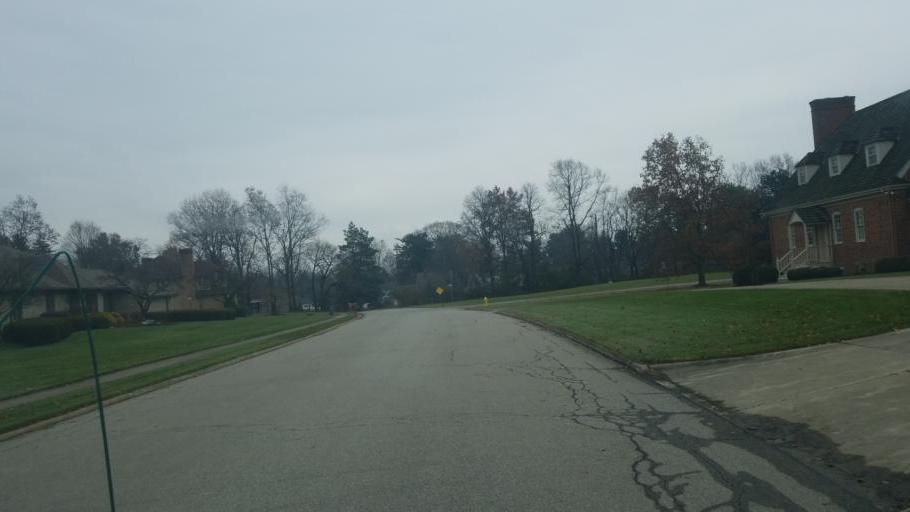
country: US
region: Ohio
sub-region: Richland County
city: Mansfield
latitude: 40.7281
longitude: -82.5435
